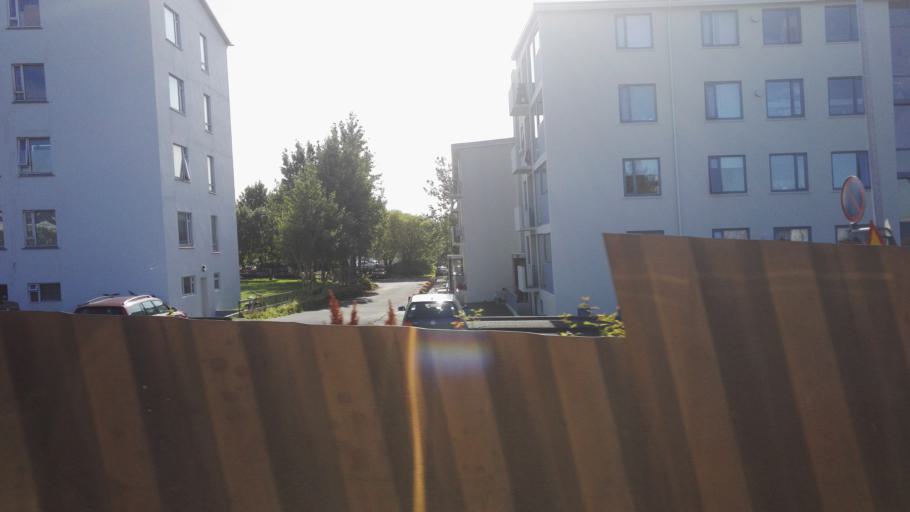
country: IS
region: Capital Region
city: Reykjavik
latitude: 64.1513
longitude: -21.8793
